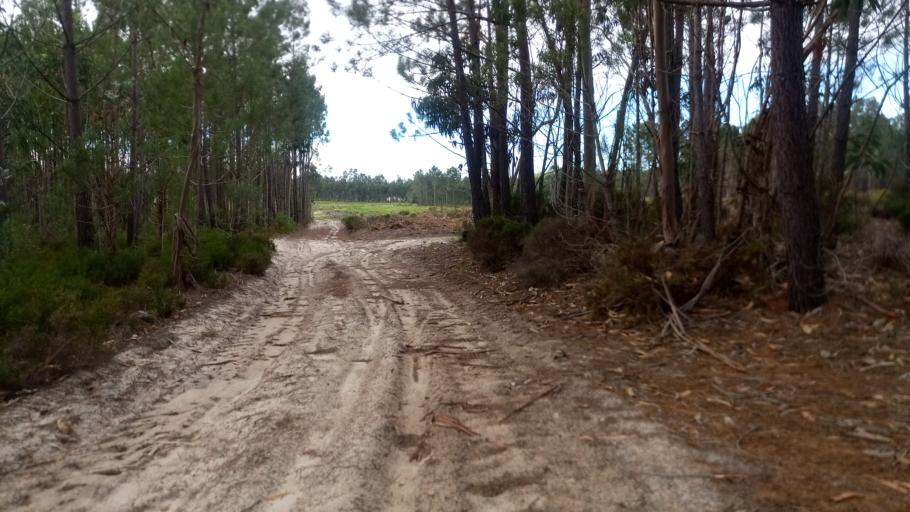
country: PT
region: Leiria
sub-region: Caldas da Rainha
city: Caldas da Rainha
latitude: 39.4489
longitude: -9.1678
